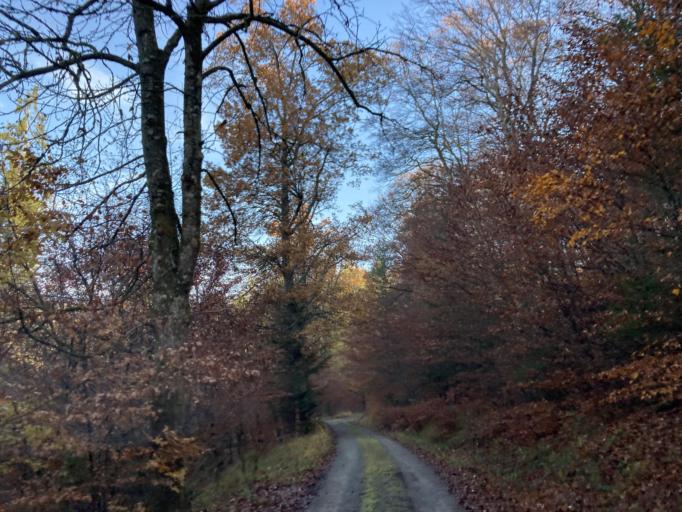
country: DE
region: Baden-Wuerttemberg
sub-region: Regierungsbezirk Stuttgart
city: Altdorf
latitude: 48.5826
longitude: 8.9984
